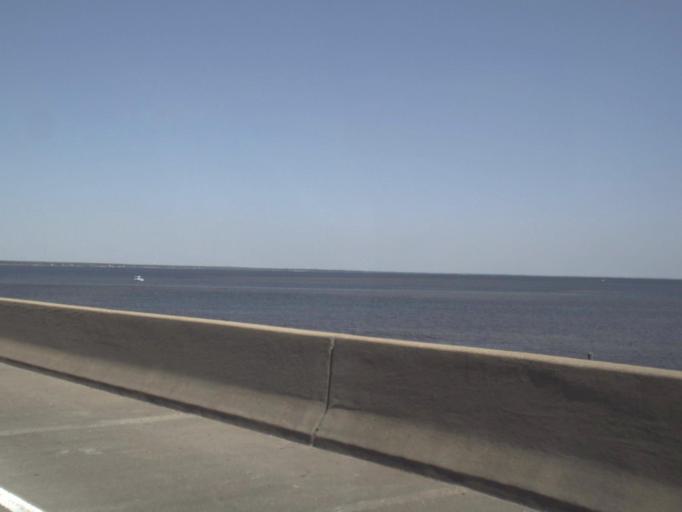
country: US
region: Florida
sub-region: Okaloosa County
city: Destin
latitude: 30.4035
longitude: -86.4255
